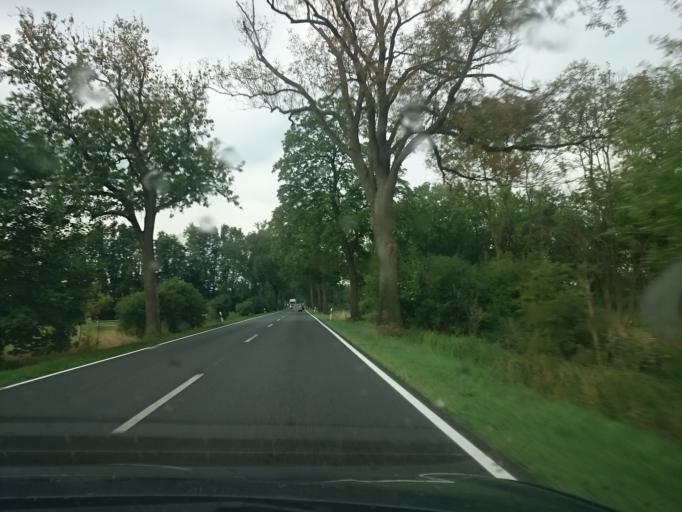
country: DE
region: Brandenburg
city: Gransee
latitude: 53.0236
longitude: 13.1848
